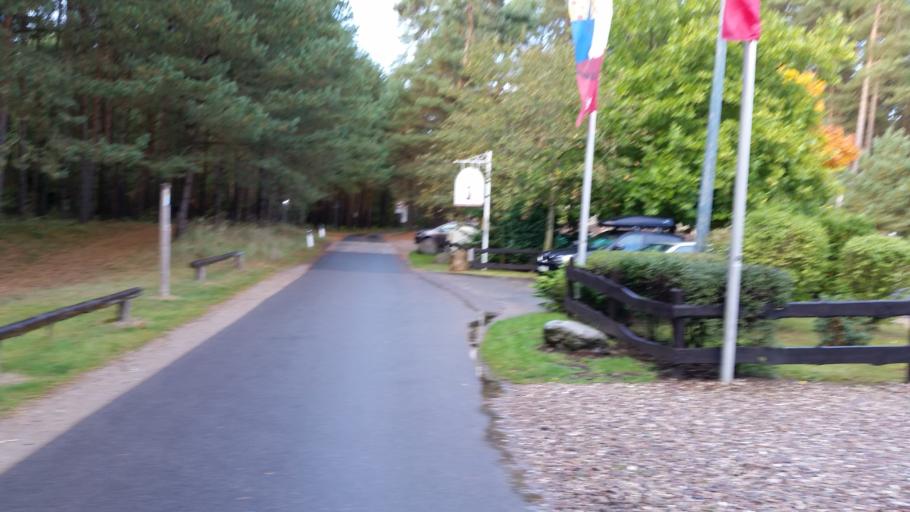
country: DE
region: Mecklenburg-Vorpommern
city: Wesenberg
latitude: 53.3013
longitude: 12.9333
